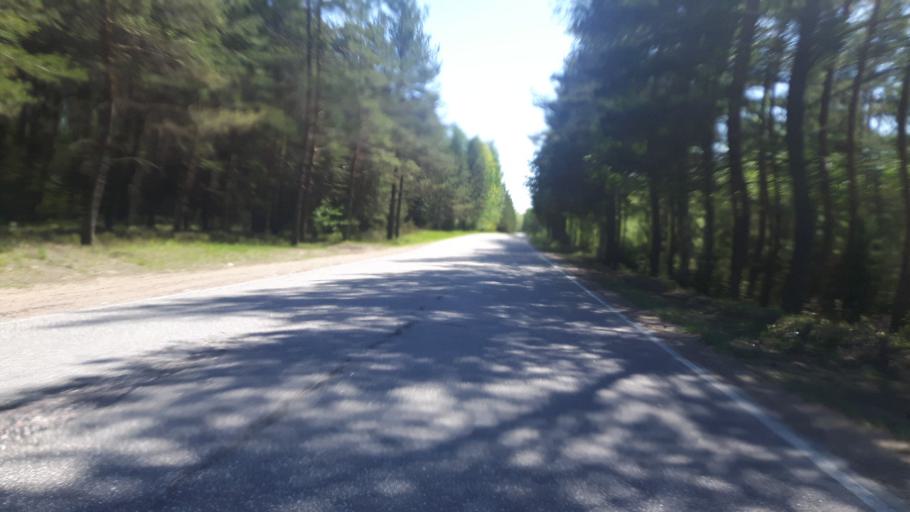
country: RU
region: Leningrad
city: Glebychevo
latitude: 60.3536
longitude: 28.8146
